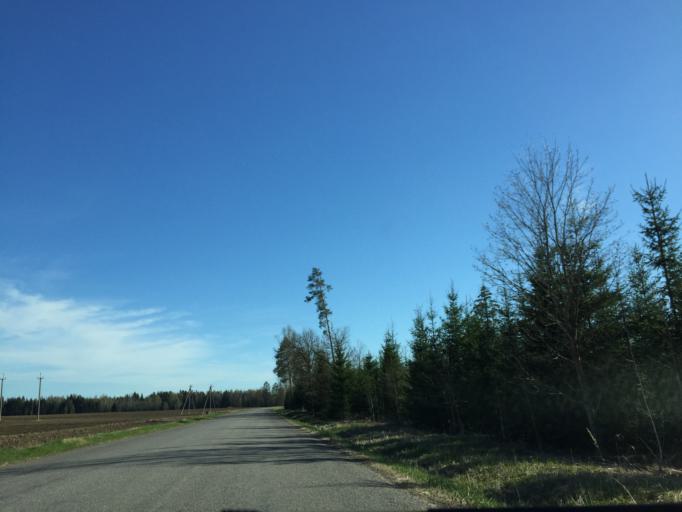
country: EE
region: Valgamaa
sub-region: Valga linn
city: Valga
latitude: 57.8574
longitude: 26.2532
